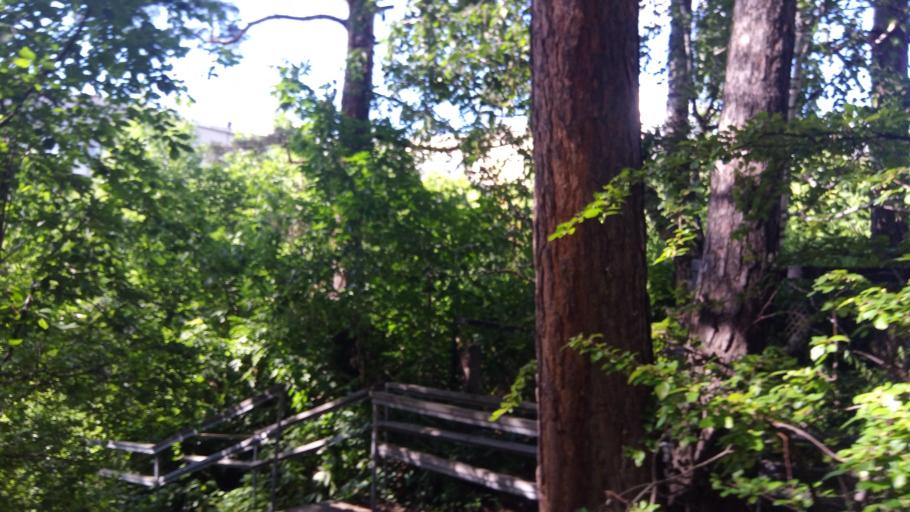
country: RU
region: Chelyabinsk
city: Chebarkul'
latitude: 55.0203
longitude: 60.3123
